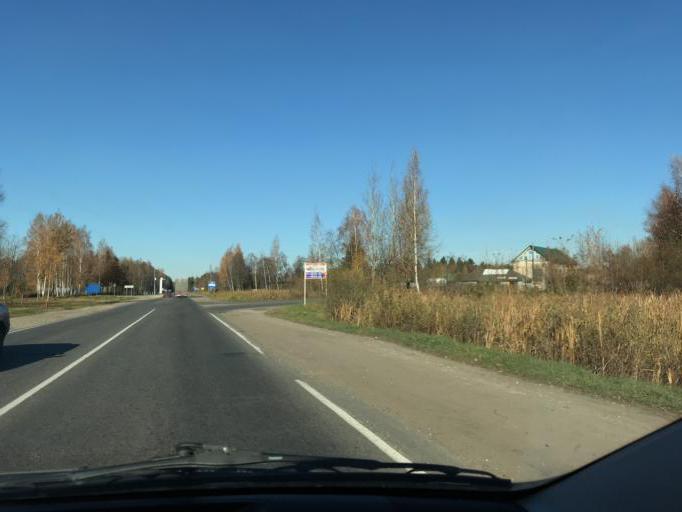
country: BY
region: Vitebsk
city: Polatsk
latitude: 55.5063
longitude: 28.7470
